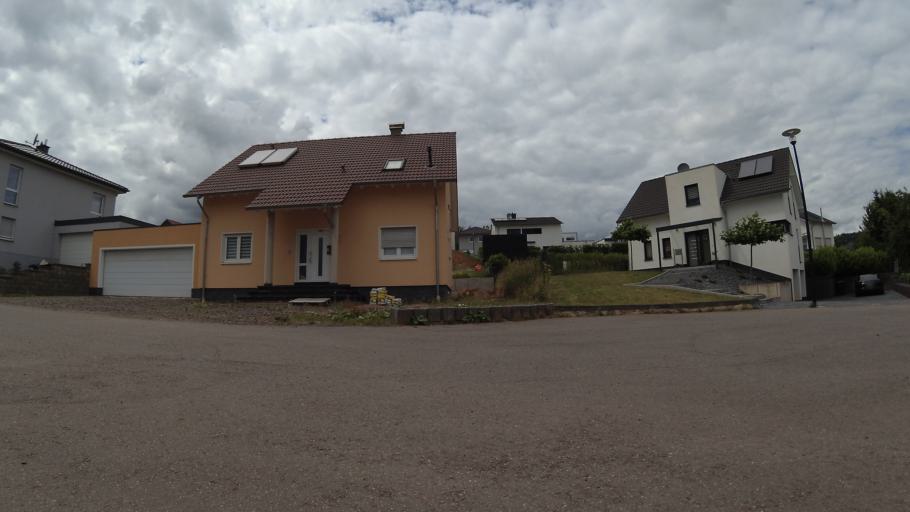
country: DE
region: Saarland
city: Nalbach
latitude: 49.3799
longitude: 6.7785
